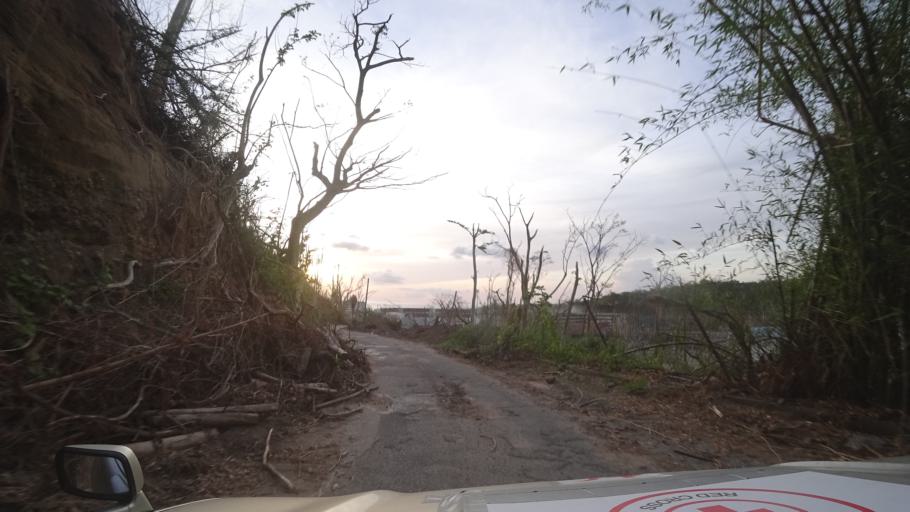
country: DM
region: Saint George
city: Roseau
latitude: 15.3009
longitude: -61.3799
